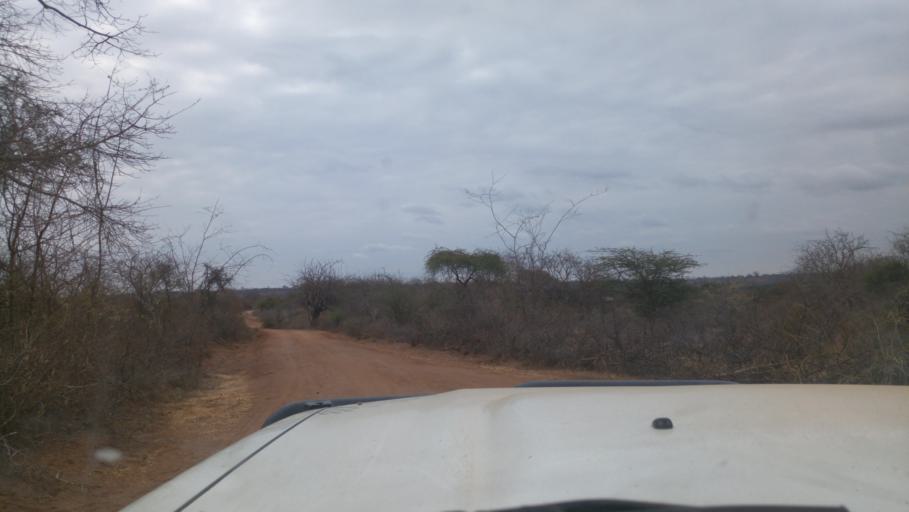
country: KE
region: Makueni
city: Makueni
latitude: -1.9955
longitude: 38.1117
